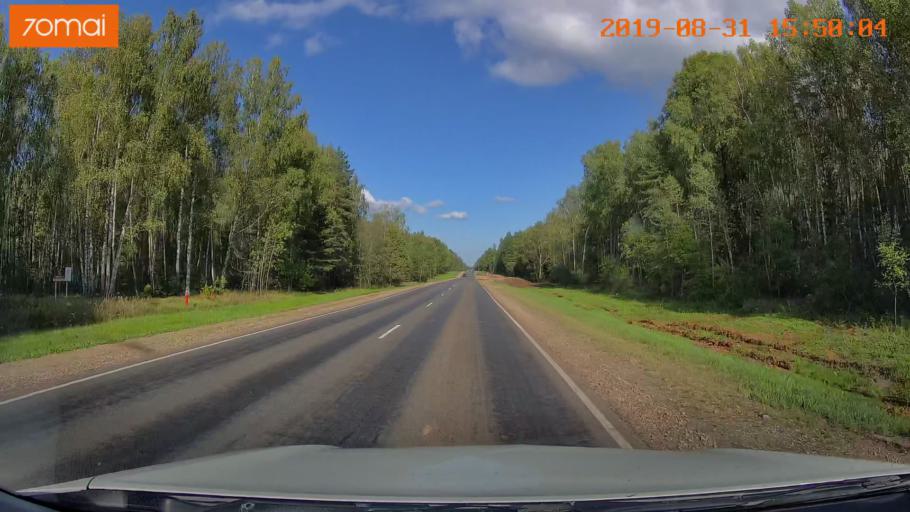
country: RU
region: Kaluga
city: Yukhnov
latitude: 54.6947
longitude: 35.0643
